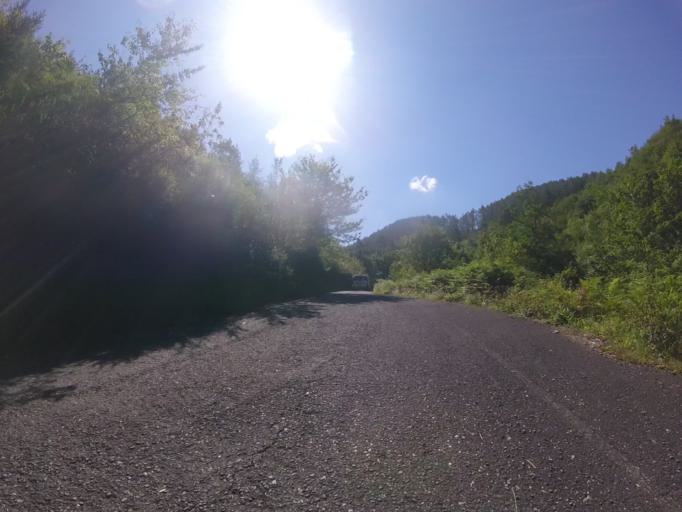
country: ES
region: Navarre
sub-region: Provincia de Navarra
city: Goizueta
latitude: 43.1864
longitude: -1.8261
